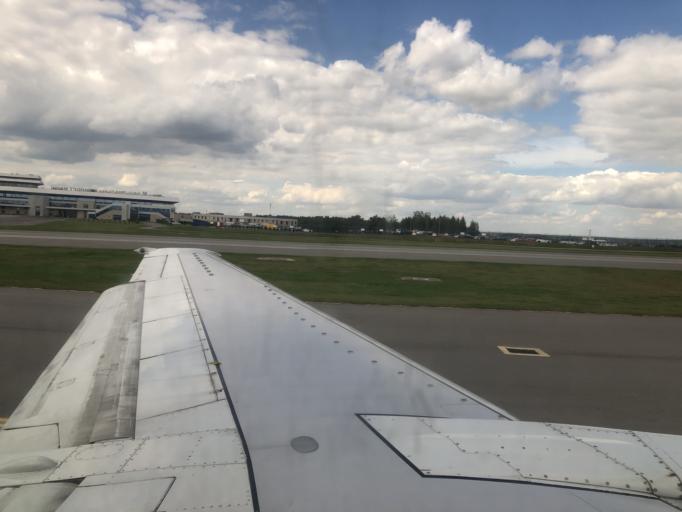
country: BY
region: Minsk
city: Smilavichy
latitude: 53.8888
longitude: 28.0421
